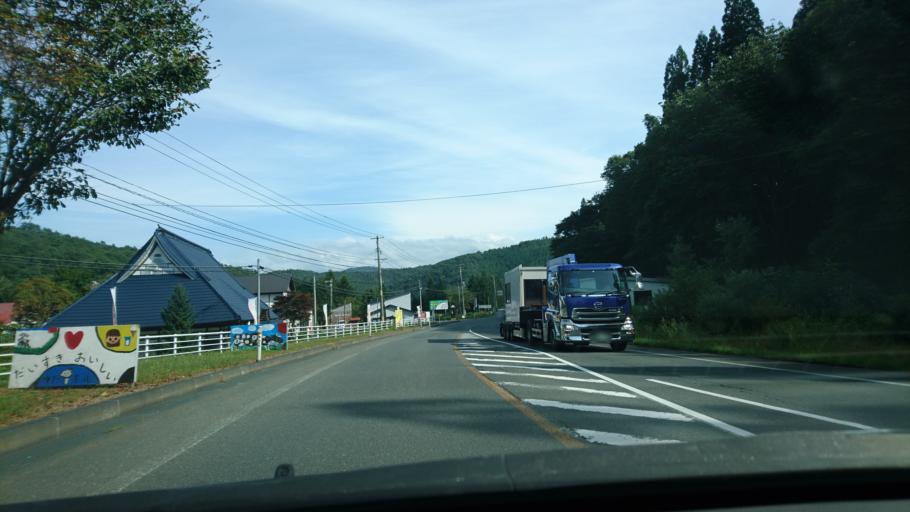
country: JP
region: Akita
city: Yokotemachi
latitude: 39.3144
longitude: 140.7564
